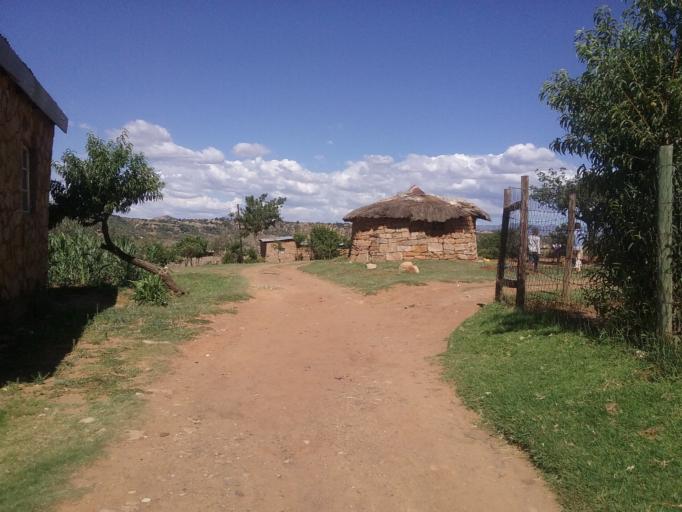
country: LS
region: Maseru
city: Maseru
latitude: -29.4155
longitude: 27.5667
